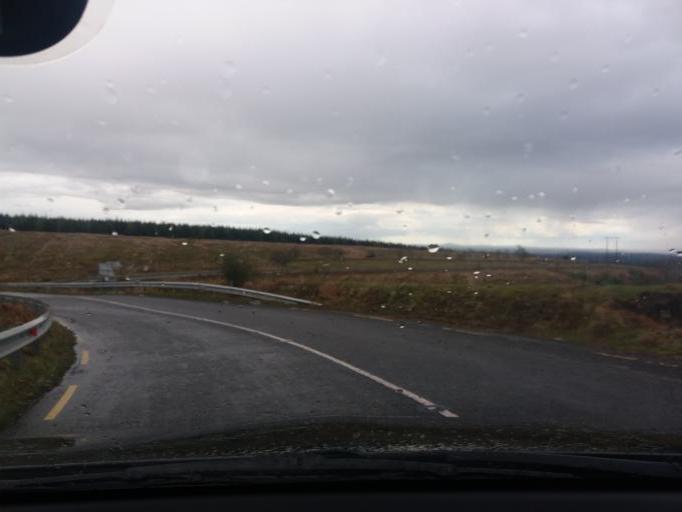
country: IE
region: Ulster
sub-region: An Cabhan
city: Ballyconnell
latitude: 54.1625
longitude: -7.7843
